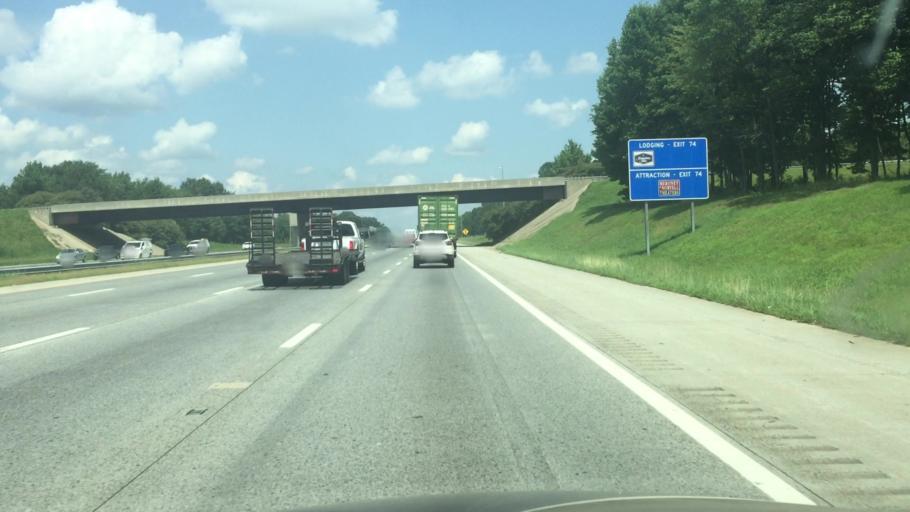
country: US
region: North Carolina
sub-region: Rowan County
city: Granite Quarry
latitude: 35.6179
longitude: -80.5096
